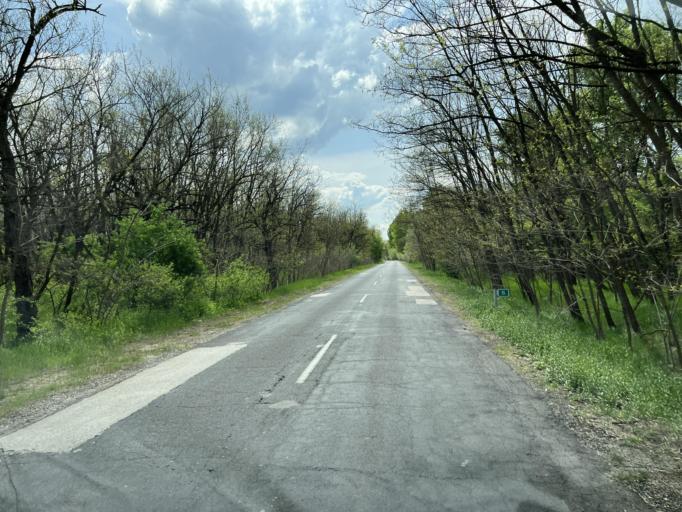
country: HU
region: Pest
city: Csemo
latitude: 47.1165
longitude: 19.6499
